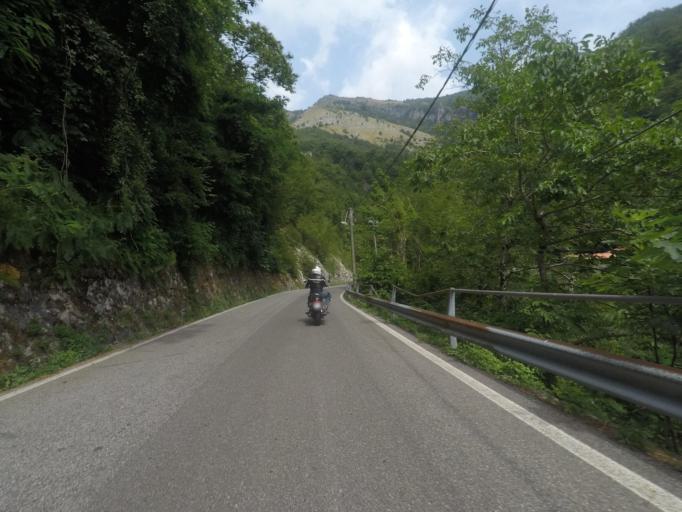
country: IT
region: Tuscany
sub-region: Provincia di Lucca
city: Careggine
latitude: 44.0651
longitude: 10.3119
